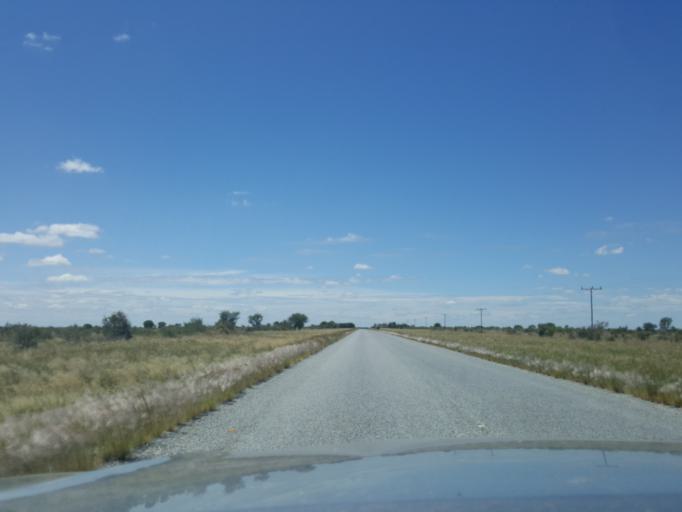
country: BW
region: Central
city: Nata
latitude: -20.1974
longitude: 26.1034
